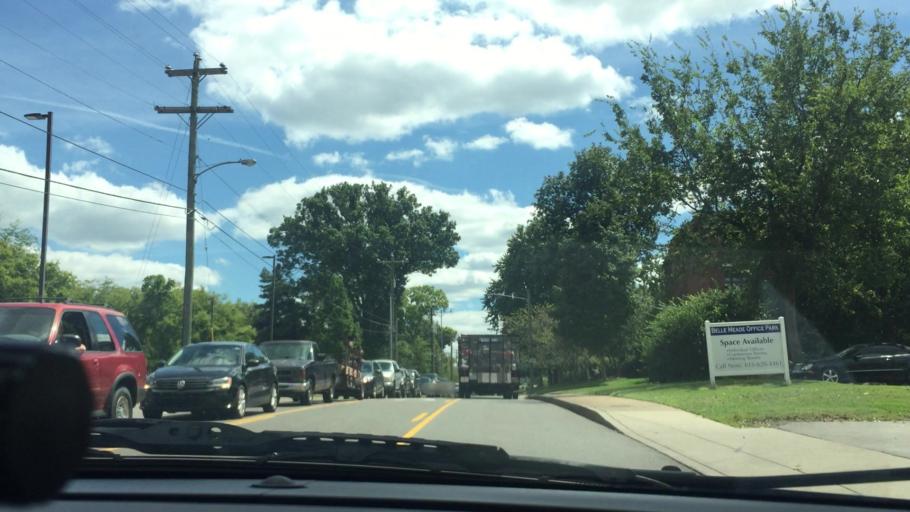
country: US
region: Tennessee
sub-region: Davidson County
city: Belle Meade
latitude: 36.1243
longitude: -86.8470
